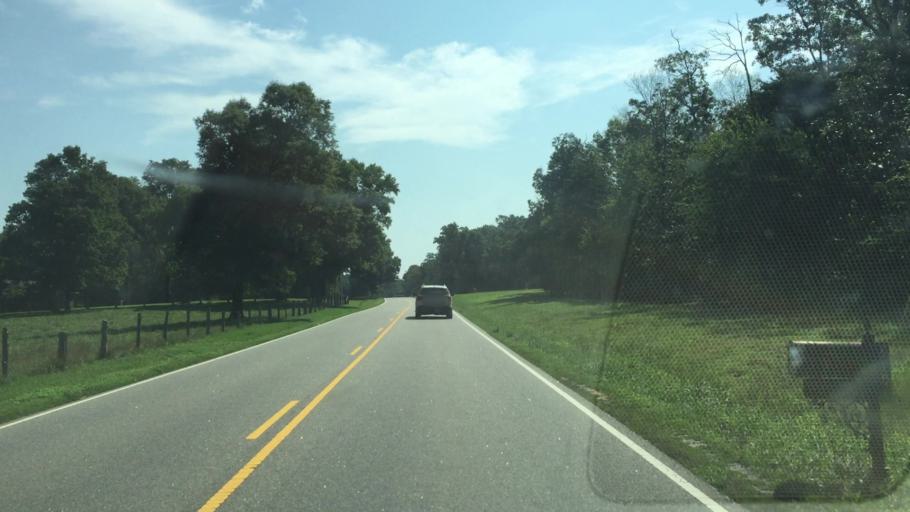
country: US
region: North Carolina
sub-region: Stanly County
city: Stanfield
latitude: 35.1320
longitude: -80.3885
